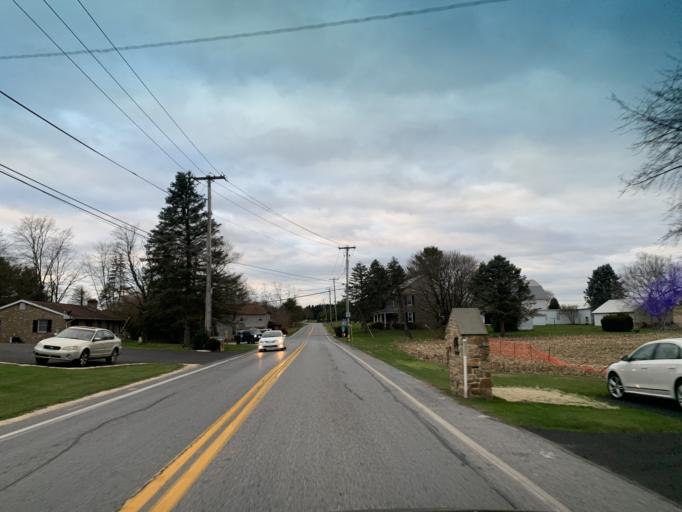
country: US
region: Pennsylvania
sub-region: York County
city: Shrewsbury
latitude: 39.7854
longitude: -76.6608
